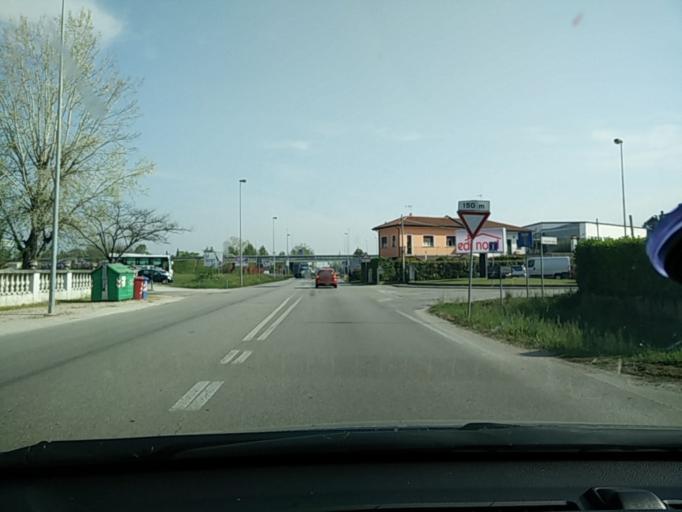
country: IT
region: Friuli Venezia Giulia
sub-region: Provincia di Pordenone
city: Pordenone
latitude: 45.9410
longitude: 12.6517
